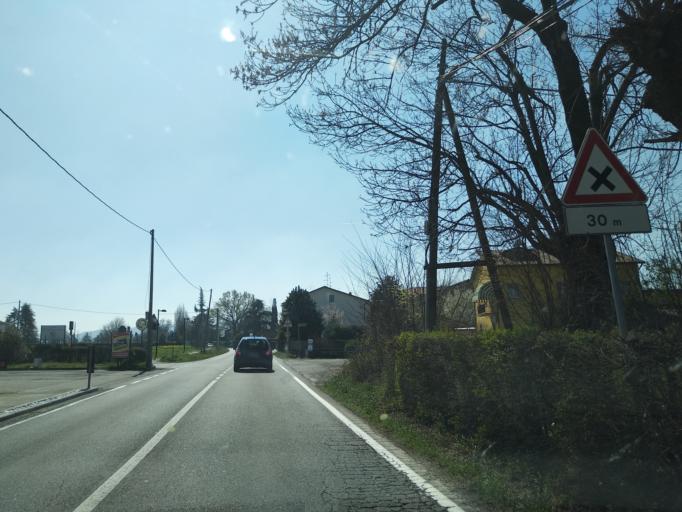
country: IT
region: Emilia-Romagna
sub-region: Provincia di Reggio Emilia
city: Albinea
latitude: 44.6474
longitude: 10.6080
